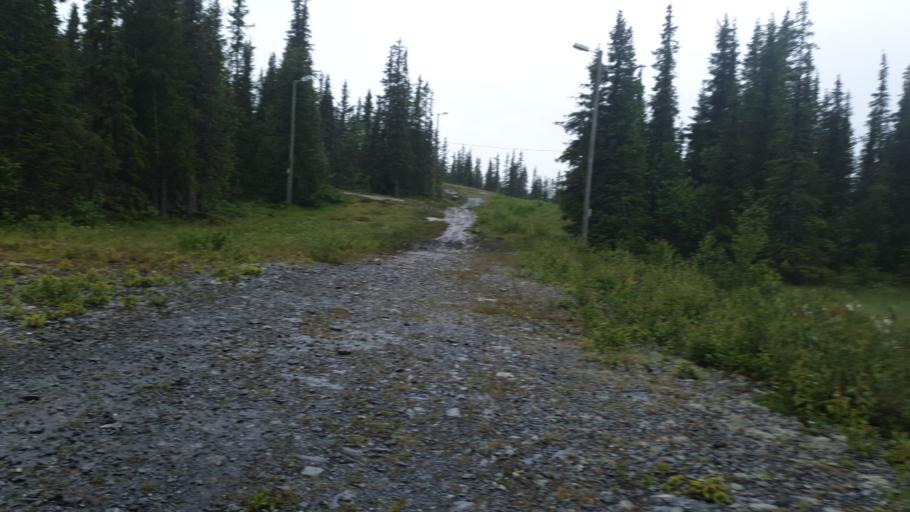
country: NO
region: Oppland
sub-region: Vestre Slidre
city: Slidre
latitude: 61.2324
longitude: 8.9130
